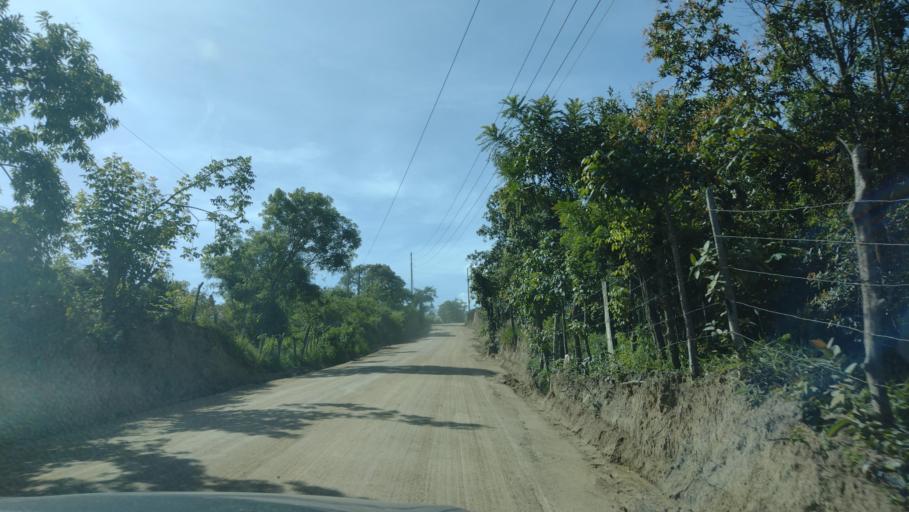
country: GT
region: Guatemala
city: Chinautla
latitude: 14.7572
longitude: -90.5210
